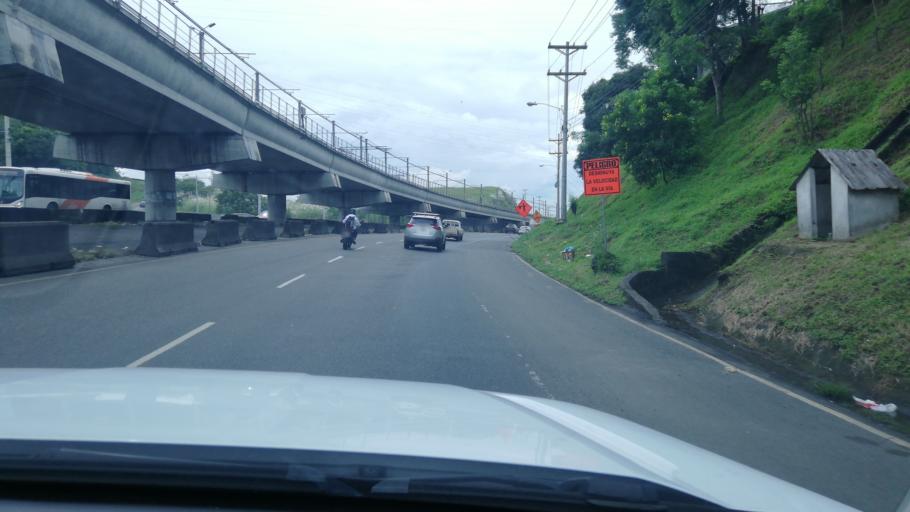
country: PA
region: Panama
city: Las Cumbres
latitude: 9.0627
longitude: -79.5104
